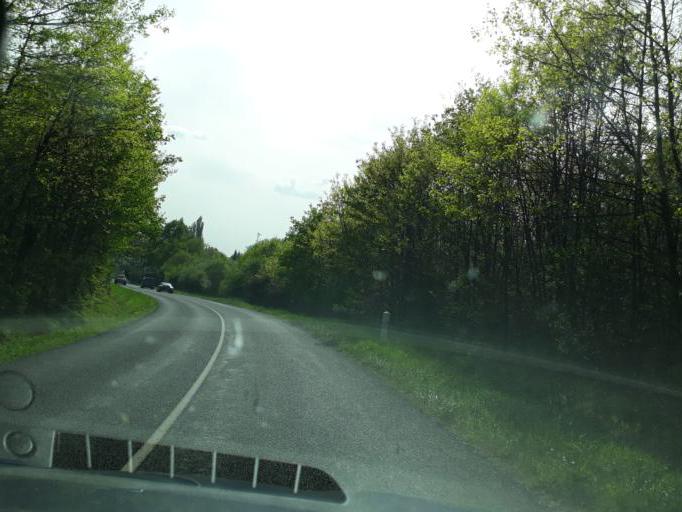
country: FR
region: Centre
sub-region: Departement du Loir-et-Cher
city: Saint-Laurent-Nouan
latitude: 47.6547
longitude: 1.6154
